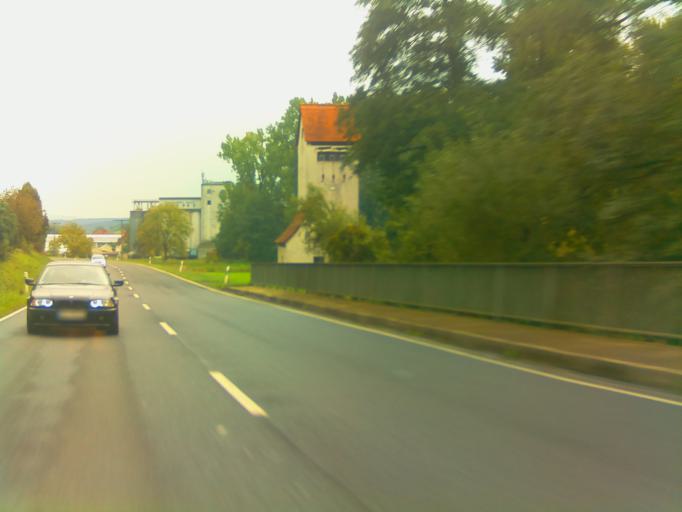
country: DE
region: Bavaria
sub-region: Regierungsbezirk Unterfranken
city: Obernburg am Main
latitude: 49.8373
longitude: 9.1063
